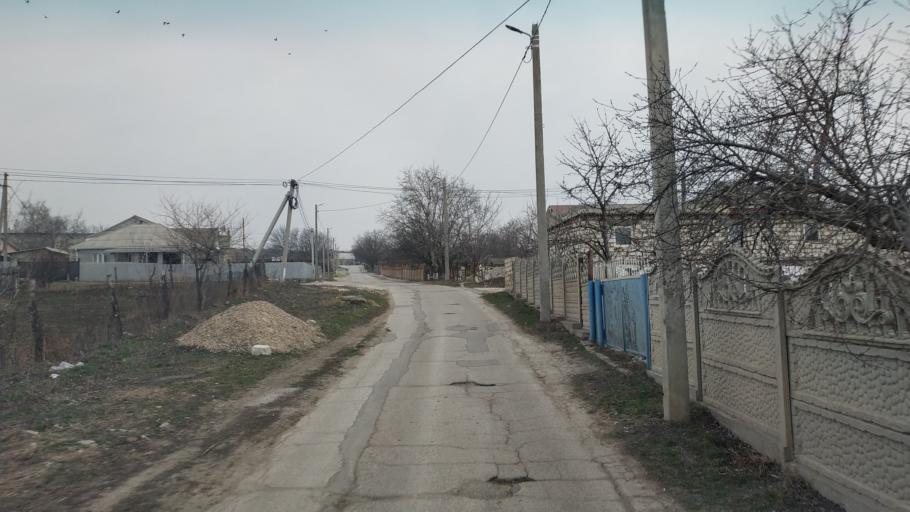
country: MD
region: Chisinau
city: Singera
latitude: 46.8202
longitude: 28.9697
